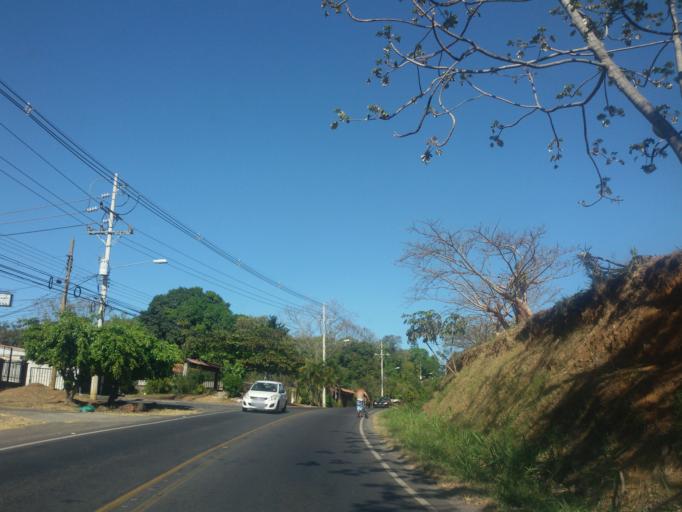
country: CR
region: Alajuela
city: Carrillos
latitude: 10.0010
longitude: -84.3064
